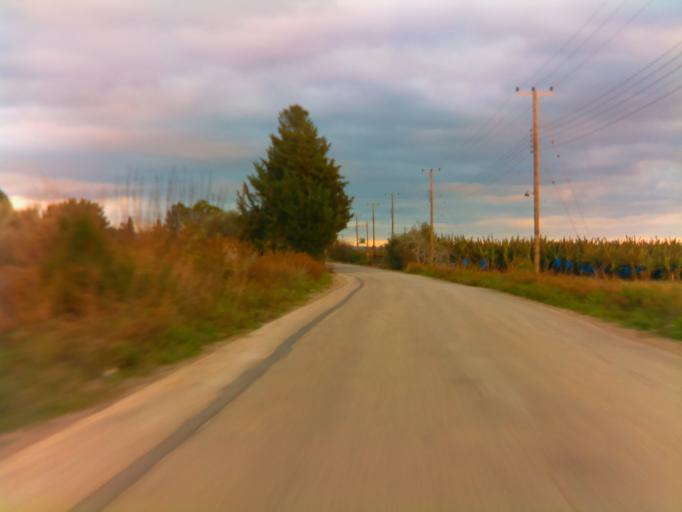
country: CY
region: Pafos
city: Pegeia
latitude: 34.8661
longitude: 32.3514
